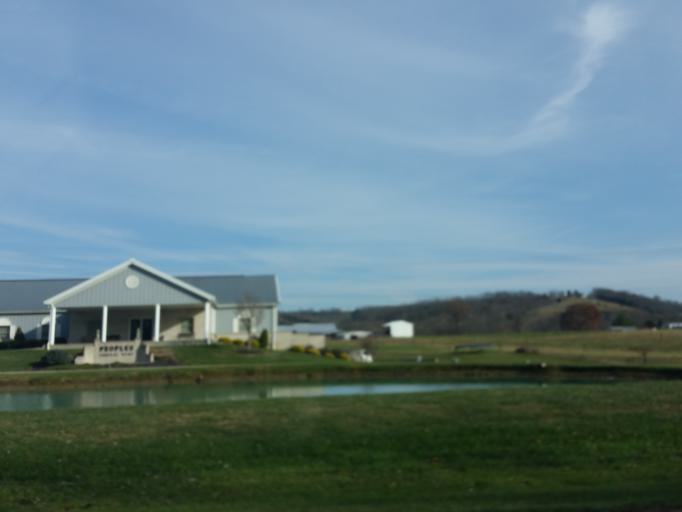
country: US
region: Kentucky
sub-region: Pendleton County
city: Falmouth
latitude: 38.7655
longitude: -84.3529
